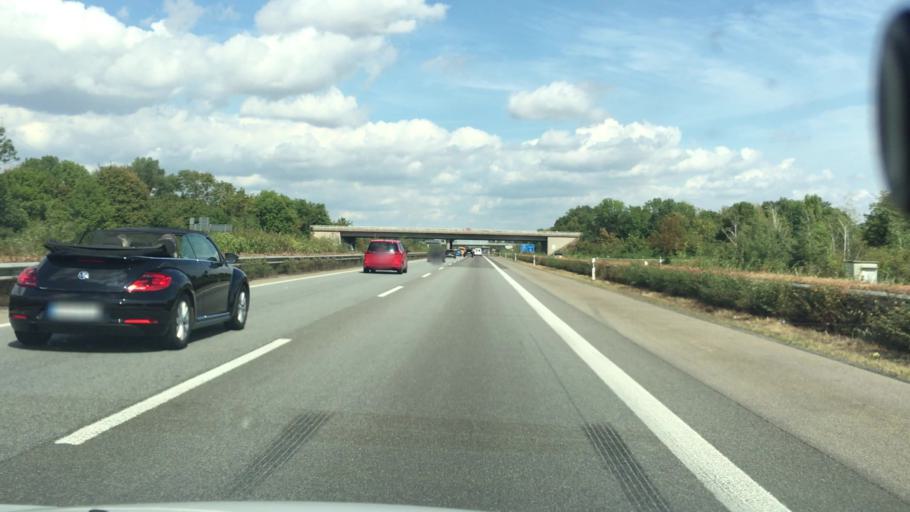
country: DE
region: Rheinland-Pfalz
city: Fussgonheim
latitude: 49.4748
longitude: 8.3127
